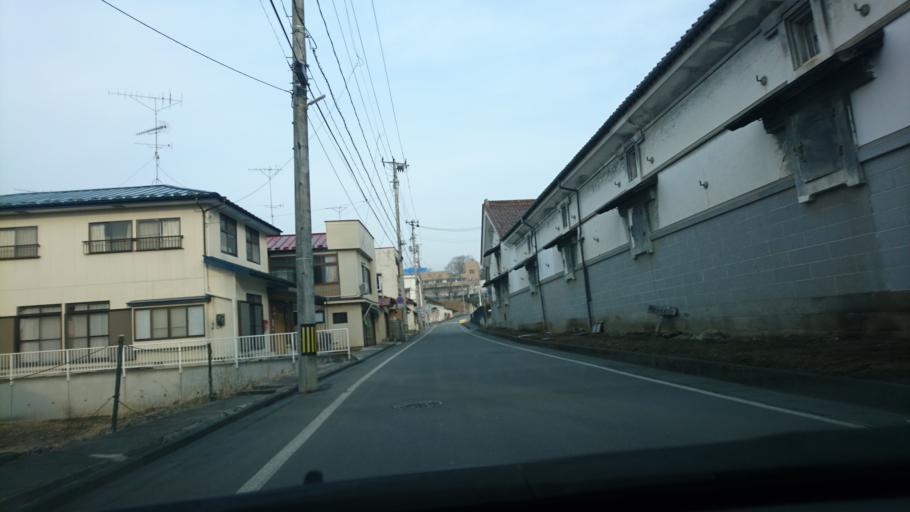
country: JP
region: Iwate
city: Ichinoseki
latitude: 38.9194
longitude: 141.3329
